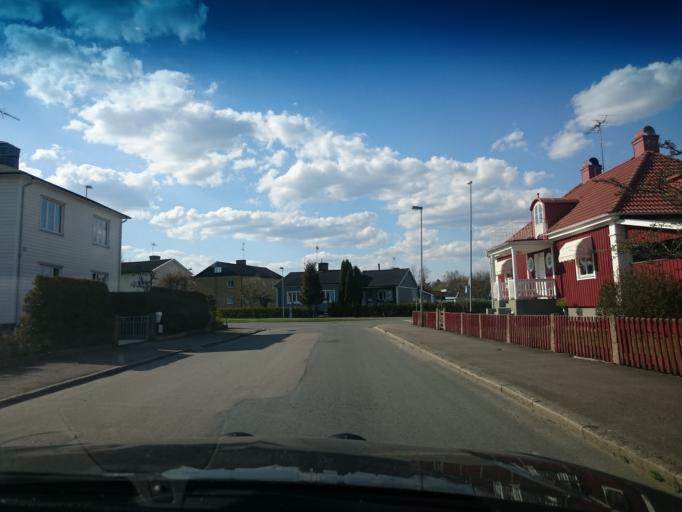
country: SE
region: Joenkoeping
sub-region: Vetlanda Kommun
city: Vetlanda
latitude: 57.4274
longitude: 15.0716
